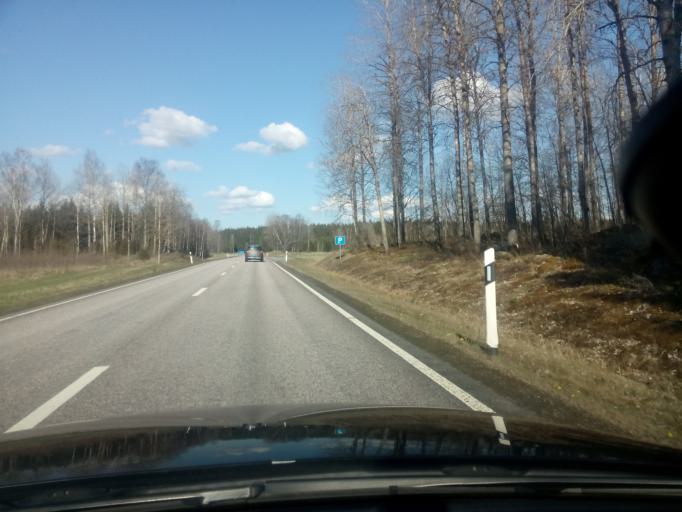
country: SE
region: Soedermanland
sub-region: Strangnas Kommun
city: Akers Styckebruk
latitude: 59.2679
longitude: 16.9601
